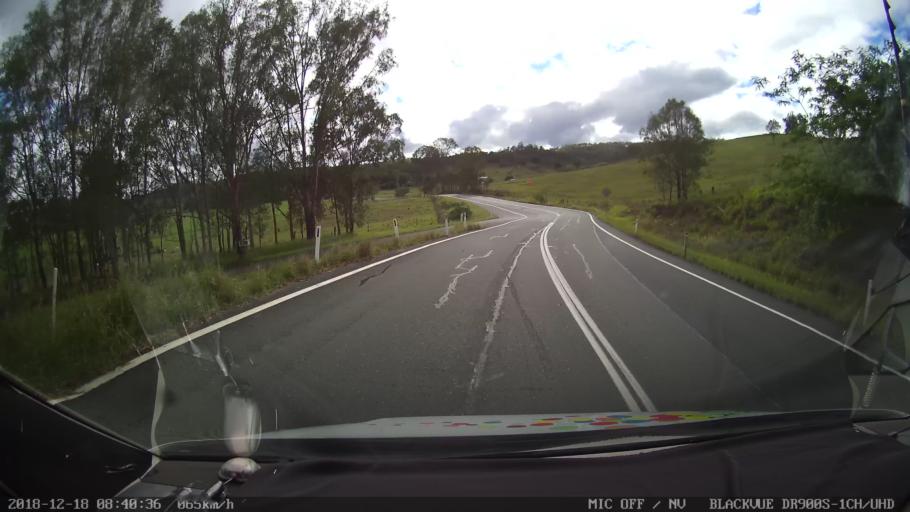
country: AU
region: Queensland
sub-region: Logan
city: Cedar Vale
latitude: -28.2412
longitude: 152.8485
